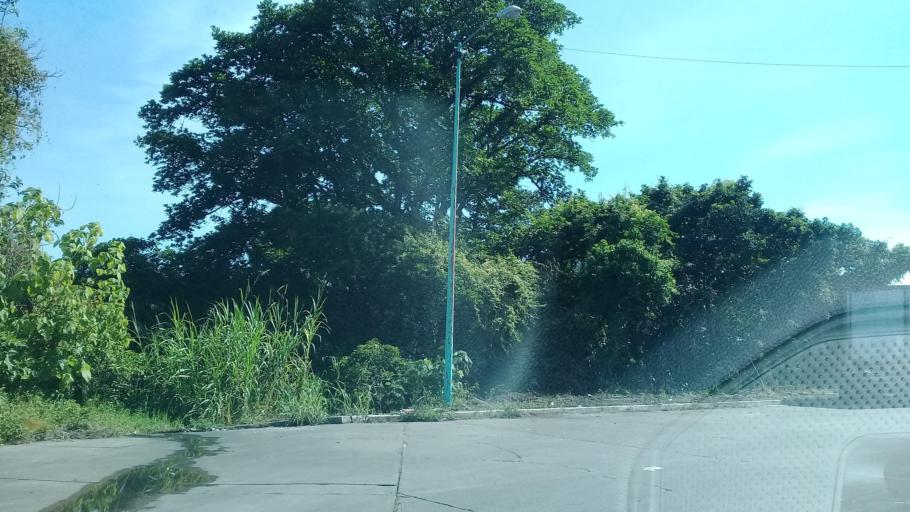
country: MX
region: Veracruz
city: Amatlan de los Reyes
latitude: 18.8580
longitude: -96.9103
